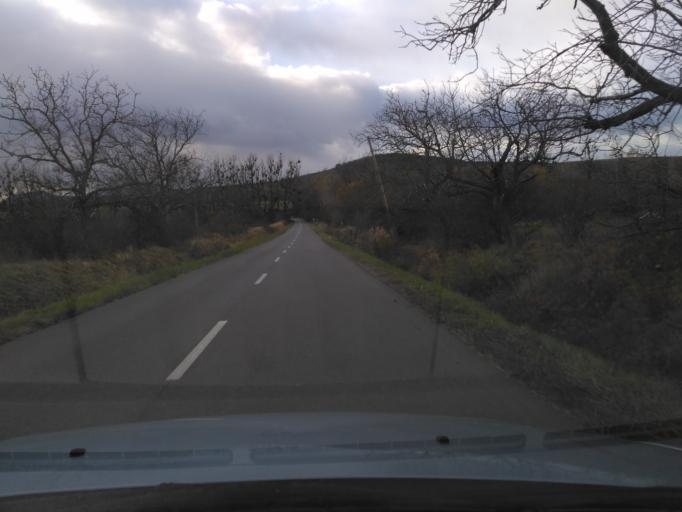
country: HU
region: Borsod-Abauj-Zemplen
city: Satoraljaujhely
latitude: 48.4283
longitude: 21.7339
